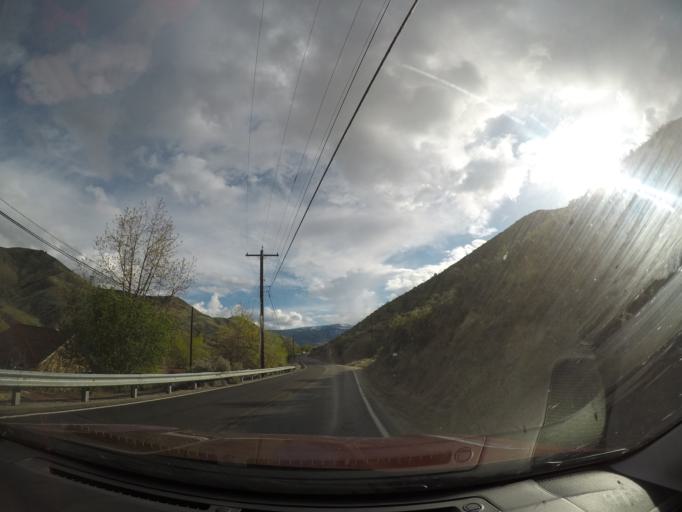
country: US
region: Washington
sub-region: Chelan County
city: South Wenatchee
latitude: 47.3856
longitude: -120.3111
